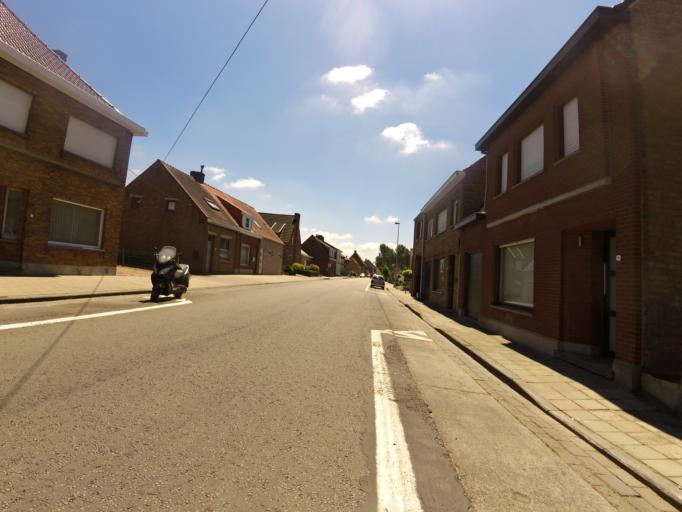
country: BE
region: Flanders
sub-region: Provincie West-Vlaanderen
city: Ichtegem
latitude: 51.1240
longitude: 3.0337
